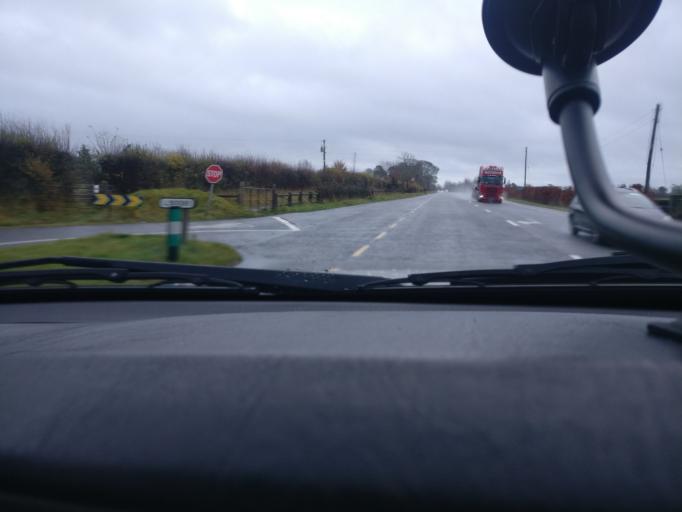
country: IE
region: Leinster
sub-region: An Mhi
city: Longwood
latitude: 53.4278
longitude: -6.9108
